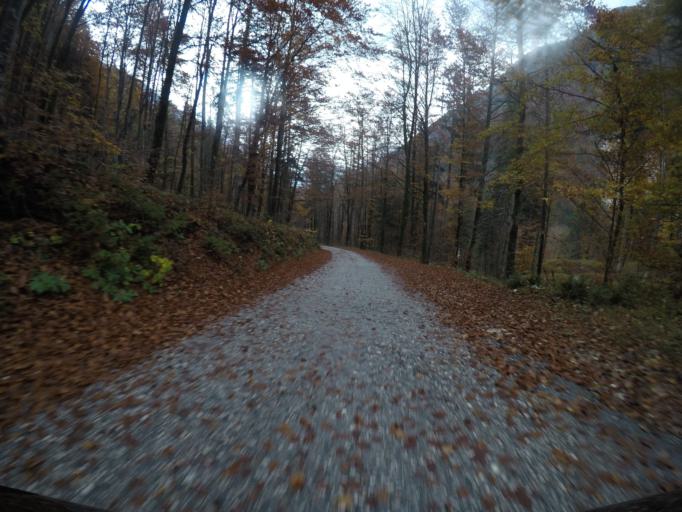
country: SI
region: Kranjska Gora
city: Mojstrana
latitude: 46.4357
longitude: 13.8891
